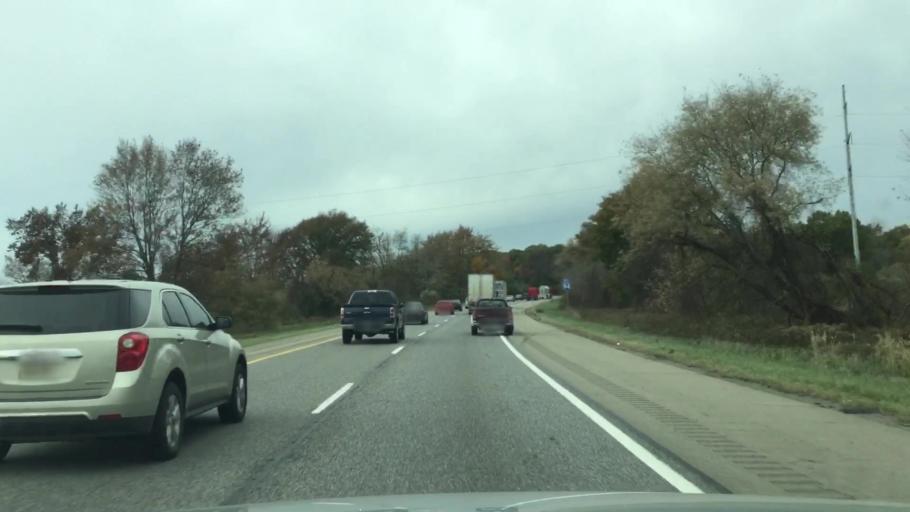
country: US
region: Michigan
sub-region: Washtenaw County
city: Chelsea
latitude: 42.2921
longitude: -84.0761
